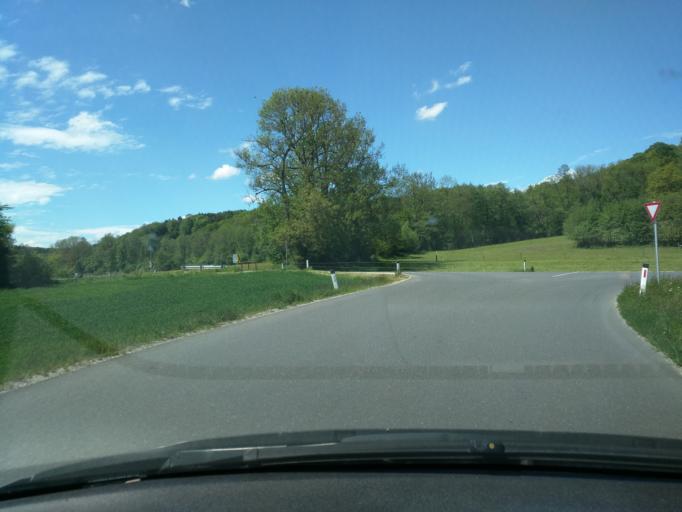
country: AT
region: Lower Austria
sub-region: Politischer Bezirk Amstetten
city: Sankt Georgen am Ybbsfelde
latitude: 48.1261
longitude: 14.9137
